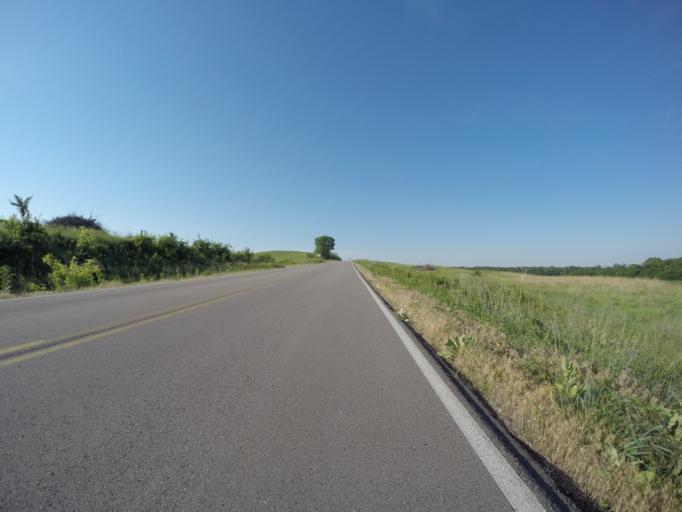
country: US
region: Nebraska
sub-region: Gage County
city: Wymore
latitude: 40.1019
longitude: -96.5016
